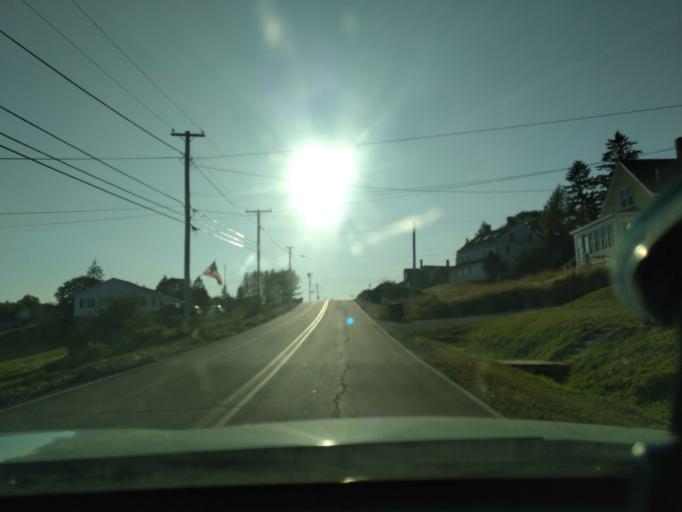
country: US
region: Maine
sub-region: Washington County
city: Machiasport
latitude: 44.6579
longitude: -67.2090
